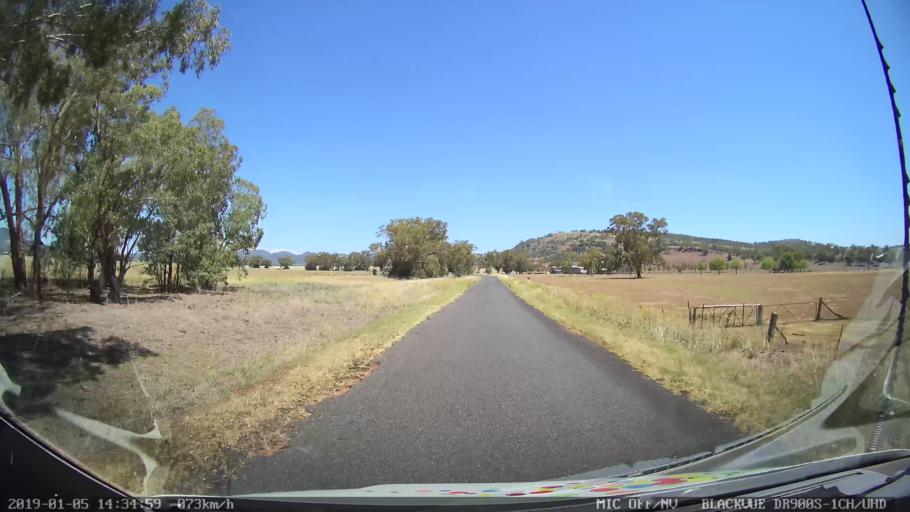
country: AU
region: New South Wales
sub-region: Tamworth Municipality
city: Phillip
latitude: -31.2374
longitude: 150.6465
